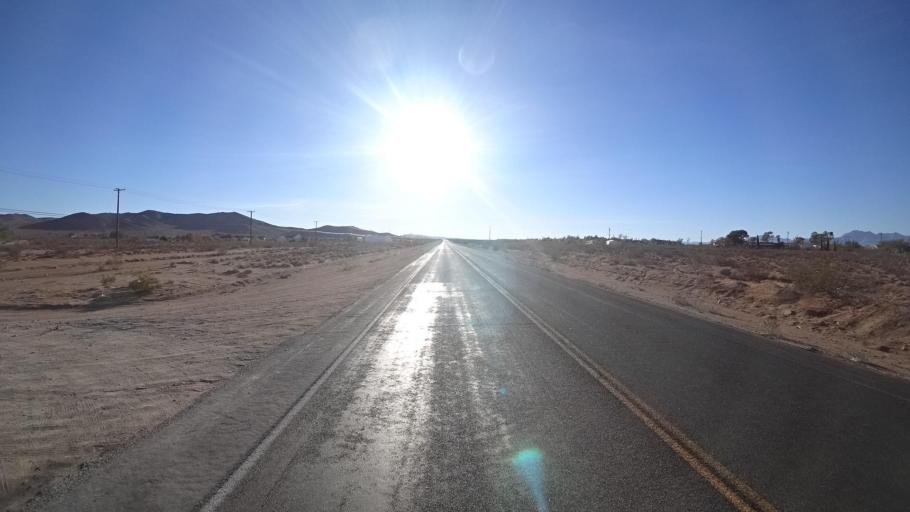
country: US
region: California
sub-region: Kern County
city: Ridgecrest
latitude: 35.5915
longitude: -117.6942
